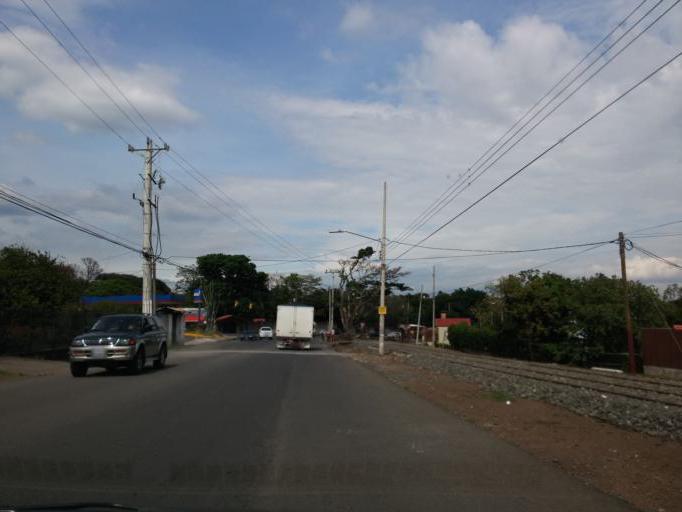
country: CR
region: Alajuela
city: Alajuela
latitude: 10.0086
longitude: -84.2092
